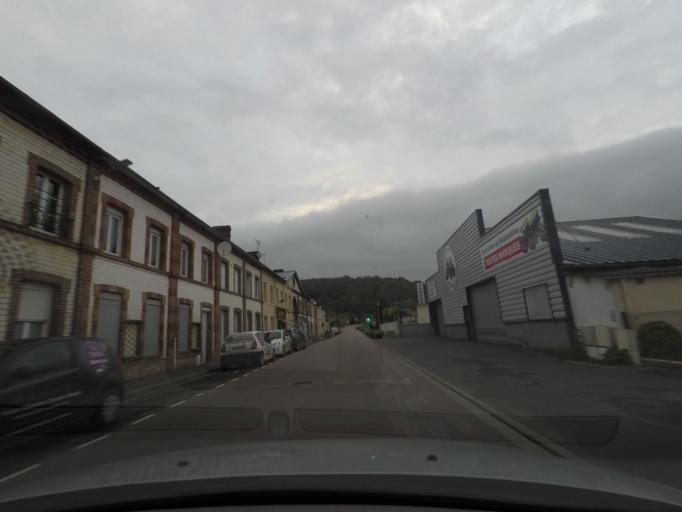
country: FR
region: Haute-Normandie
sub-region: Departement de la Seine-Maritime
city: Fontaine-le-Bourg
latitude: 49.5639
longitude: 1.1638
